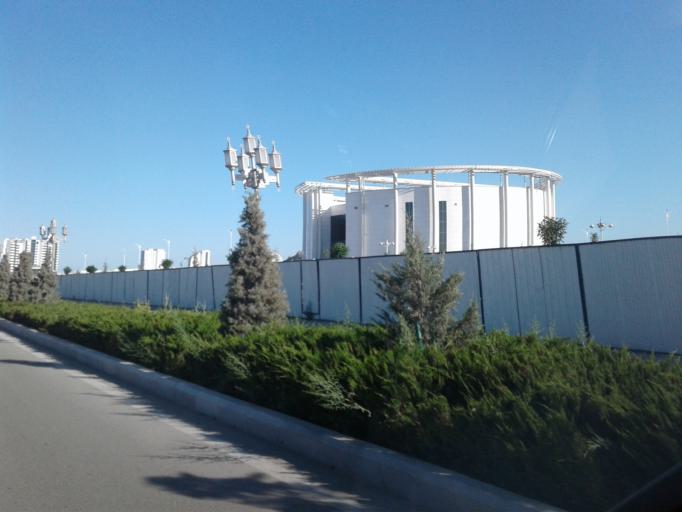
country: TM
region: Balkan
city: Turkmenbasy
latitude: 39.9607
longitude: 52.8413
